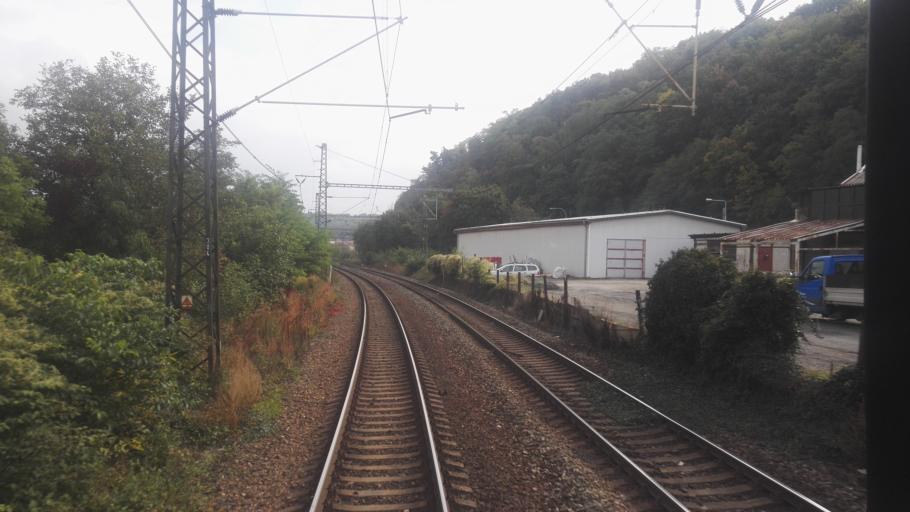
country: CZ
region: Central Bohemia
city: Kralupy nad Vltavou
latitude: 50.2450
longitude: 14.3040
